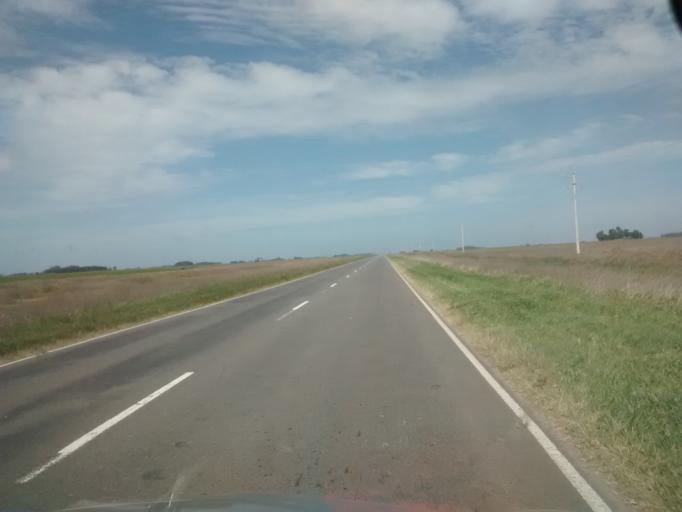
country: AR
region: Buenos Aires
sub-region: Partido de Ayacucho
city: Ayacucho
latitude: -36.9882
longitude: -58.5348
